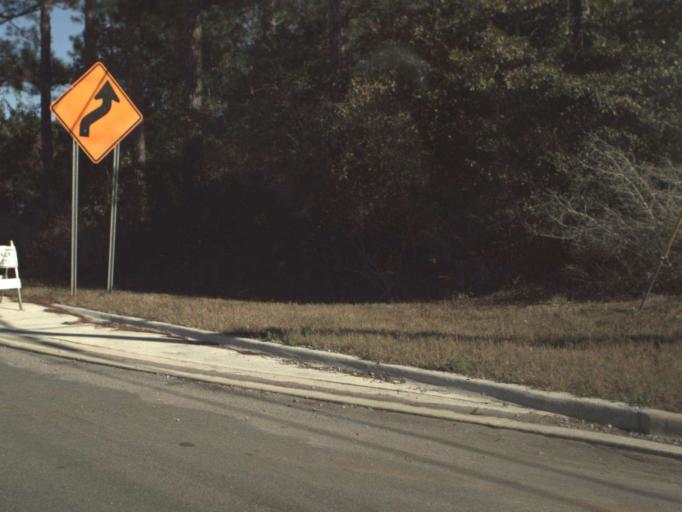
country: US
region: Florida
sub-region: Santa Rosa County
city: Bagdad
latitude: 30.5443
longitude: -87.0872
